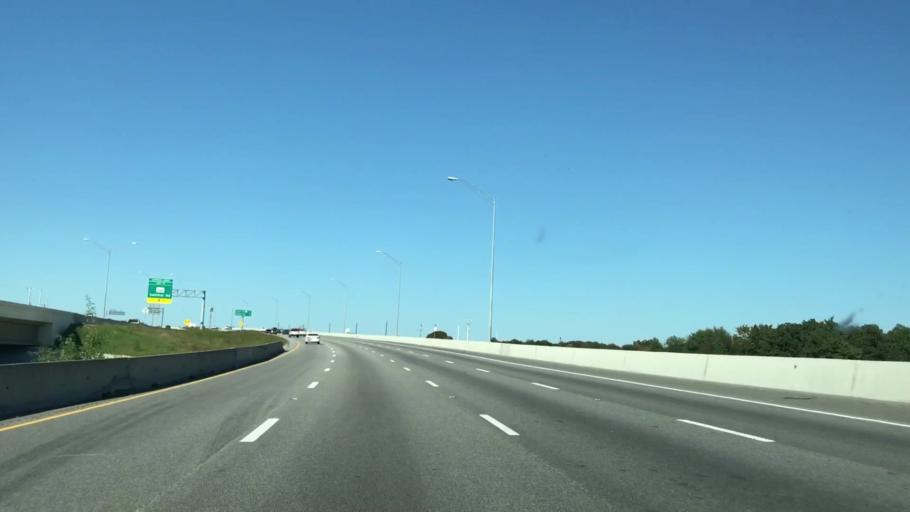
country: US
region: Texas
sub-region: Denton County
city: Lake Dallas
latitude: 33.1076
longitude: -97.0273
